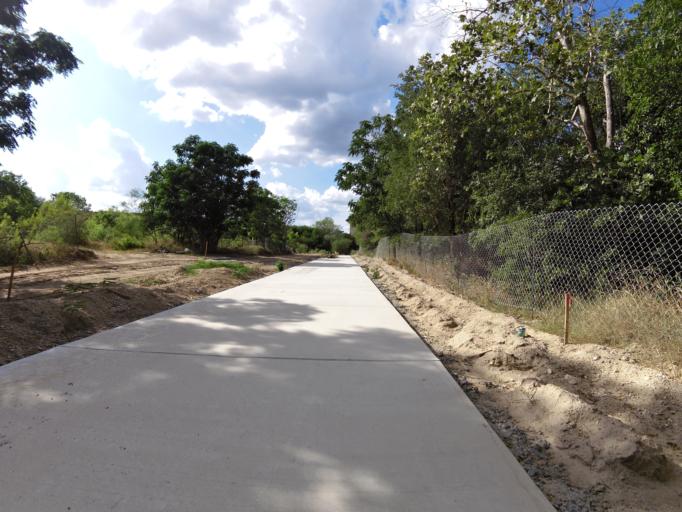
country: US
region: Texas
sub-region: Bexar County
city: Shavano Park
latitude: 29.6027
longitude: -98.6022
